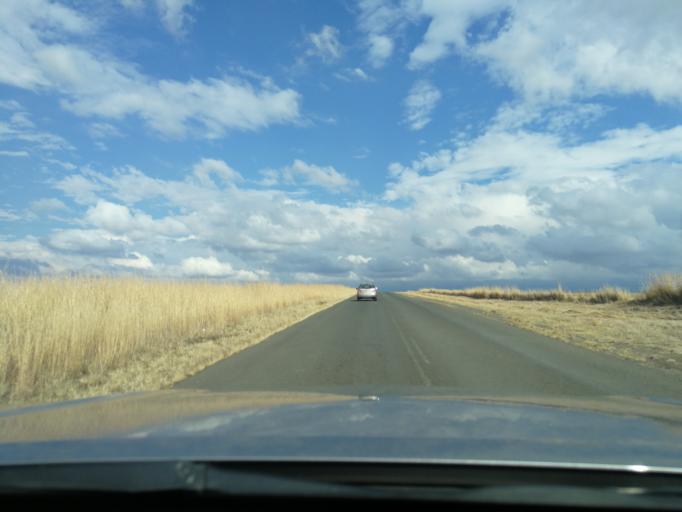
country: ZA
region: Orange Free State
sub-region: Fezile Dabi District Municipality
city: Frankfort
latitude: -27.4497
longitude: 28.5170
